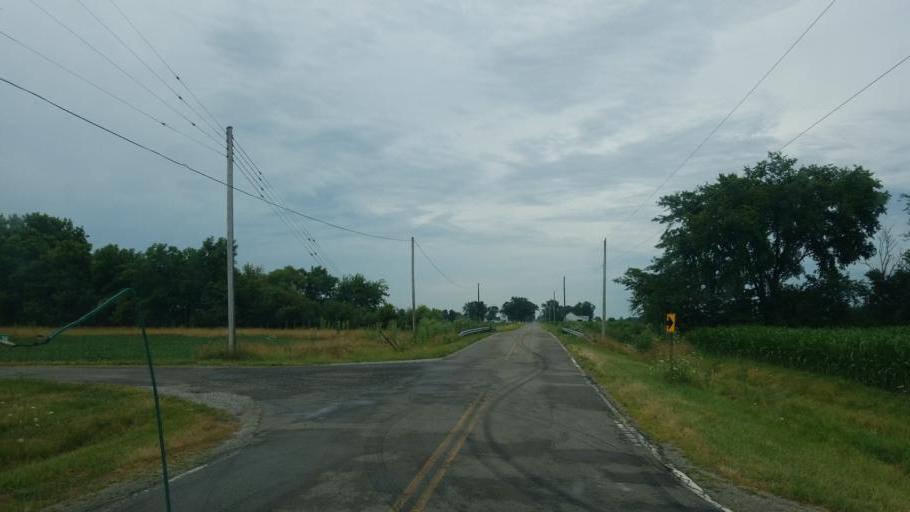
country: US
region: Ohio
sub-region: Defiance County
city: Hicksville
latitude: 41.2816
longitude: -84.6895
